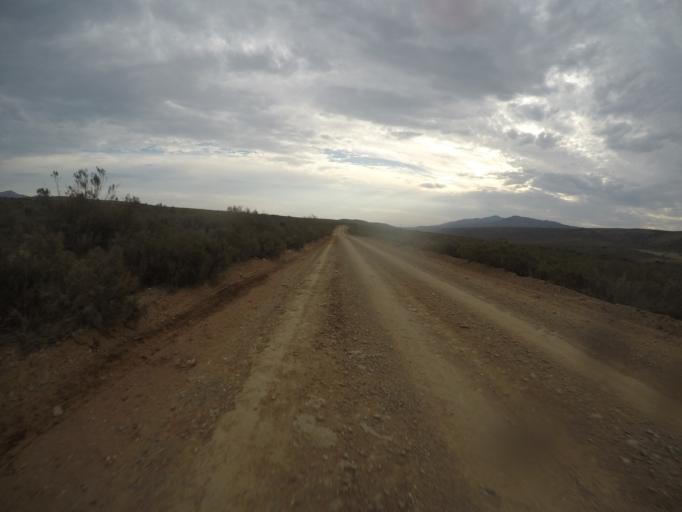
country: ZA
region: Eastern Cape
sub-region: Cacadu District Municipality
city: Willowmore
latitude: -33.4922
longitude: 23.5831
